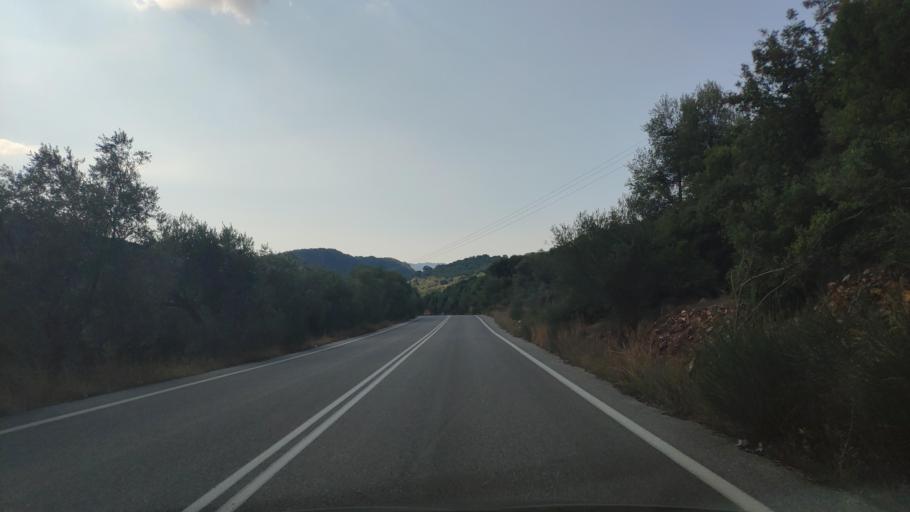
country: GR
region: West Greece
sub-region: Nomos Aitolias kai Akarnanias
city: Stanos
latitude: 38.7708
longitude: 21.1580
